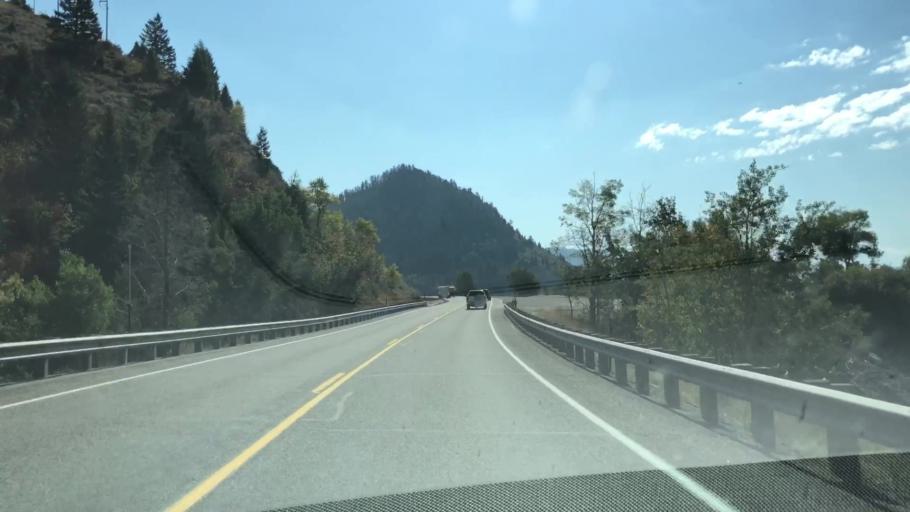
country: US
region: Idaho
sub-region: Teton County
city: Victor
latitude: 43.3200
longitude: -111.1567
